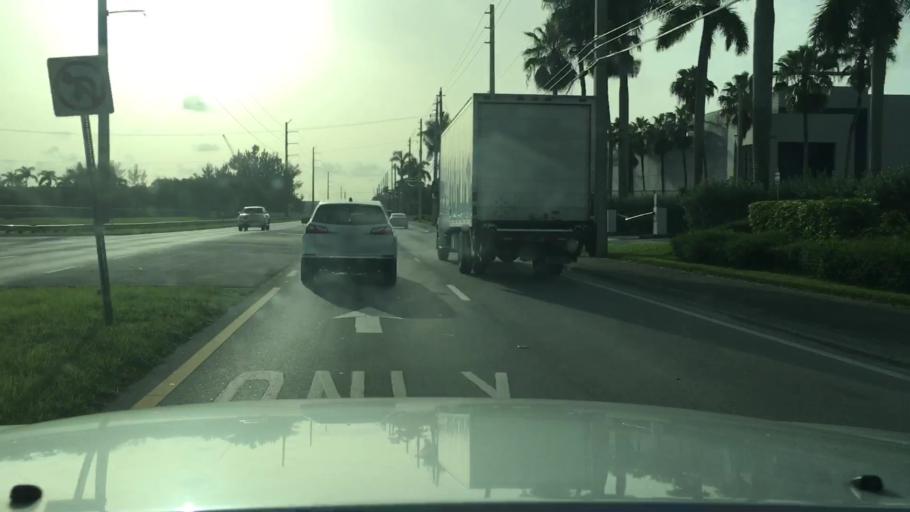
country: US
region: Florida
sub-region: Miami-Dade County
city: Sweetwater
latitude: 25.7966
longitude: -80.3838
